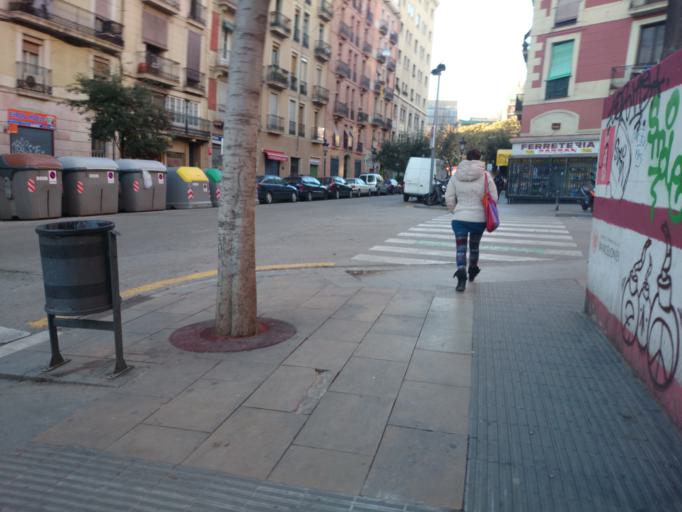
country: ES
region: Catalonia
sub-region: Provincia de Barcelona
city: Ciutat Vella
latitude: 41.3759
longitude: 2.1686
